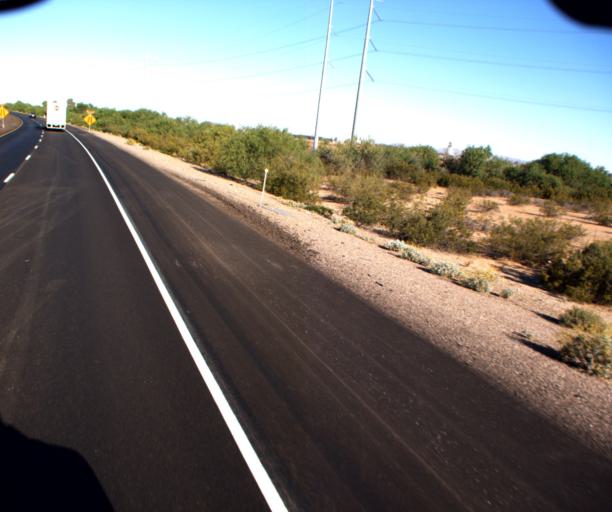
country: US
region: Arizona
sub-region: Pinal County
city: Casa Grande
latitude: 32.8338
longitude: -111.7109
